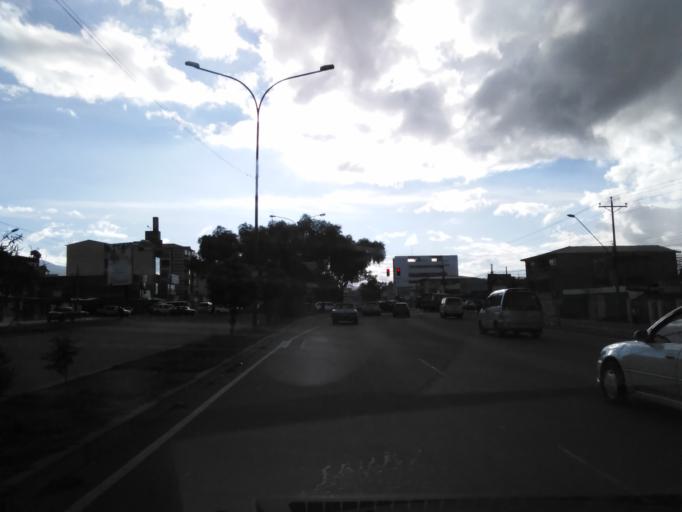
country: BO
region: Cochabamba
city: Cochabamba
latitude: -17.3939
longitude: -66.1716
